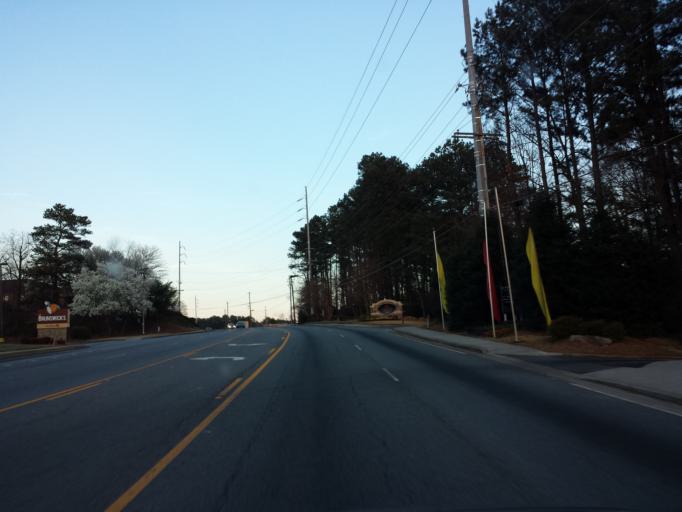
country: US
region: Georgia
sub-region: Cobb County
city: Smyrna
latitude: 33.9228
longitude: -84.4743
